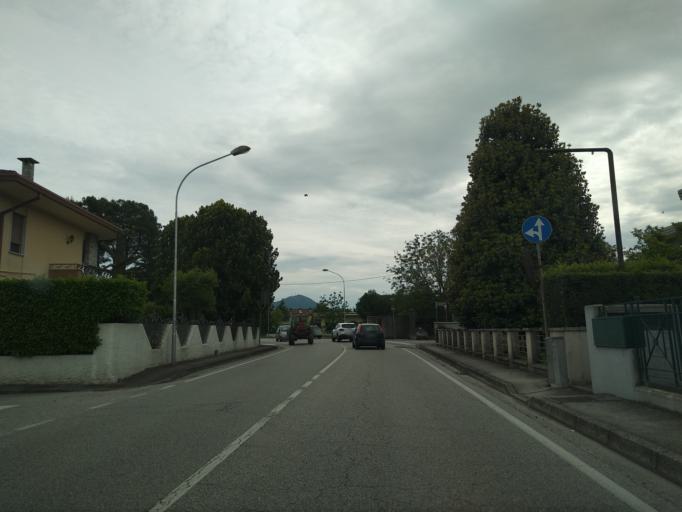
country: IT
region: Veneto
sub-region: Provincia di Padova
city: Cervarese Santa Croce
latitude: 45.4236
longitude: 11.6893
